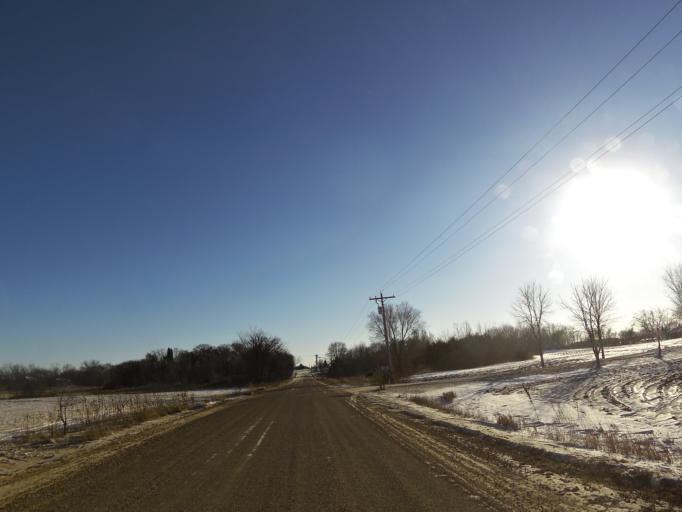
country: US
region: Minnesota
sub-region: Le Sueur County
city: New Prague
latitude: 44.5474
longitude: -93.5530
